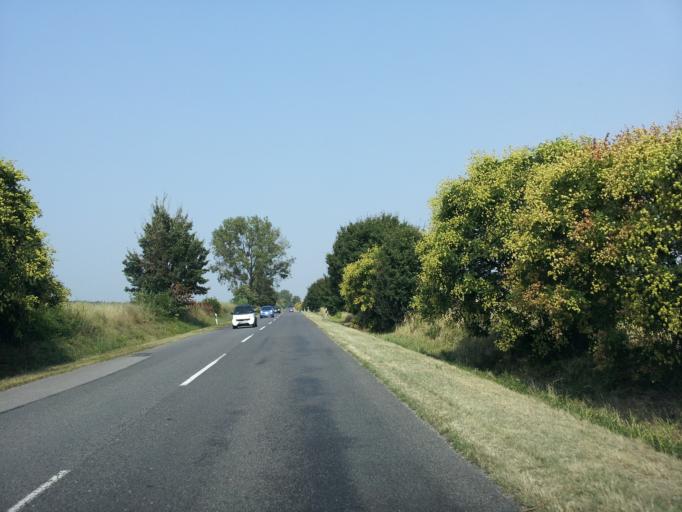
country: HU
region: Gyor-Moson-Sopron
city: Pannonhalma
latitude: 47.4770
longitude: 17.7906
